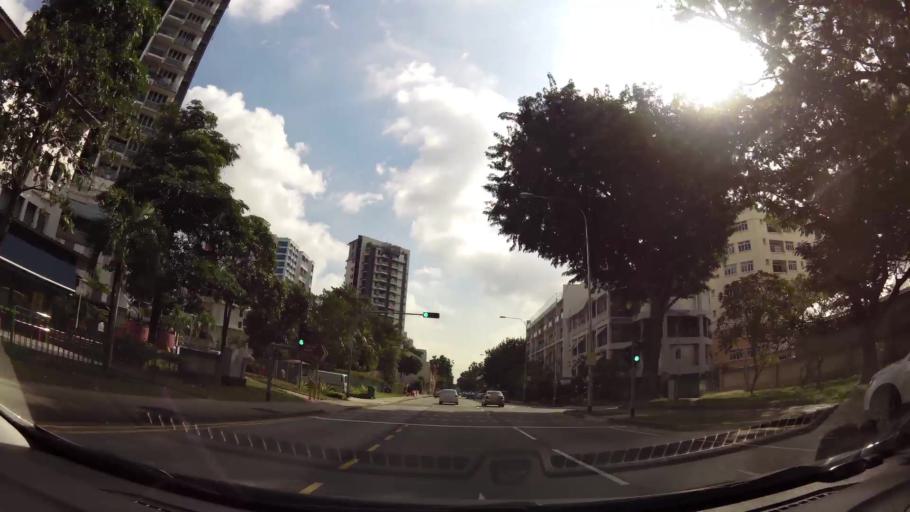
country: SG
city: Singapore
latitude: 1.3158
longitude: 103.8864
